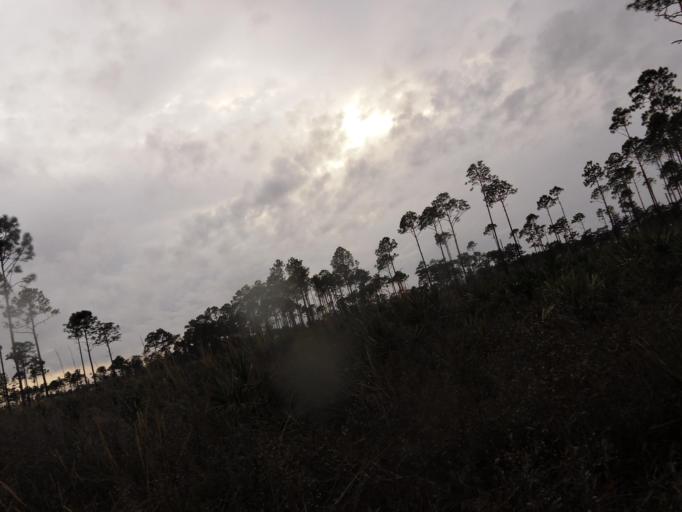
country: US
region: Florida
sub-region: Duval County
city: Atlantic Beach
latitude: 30.4770
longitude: -81.4984
